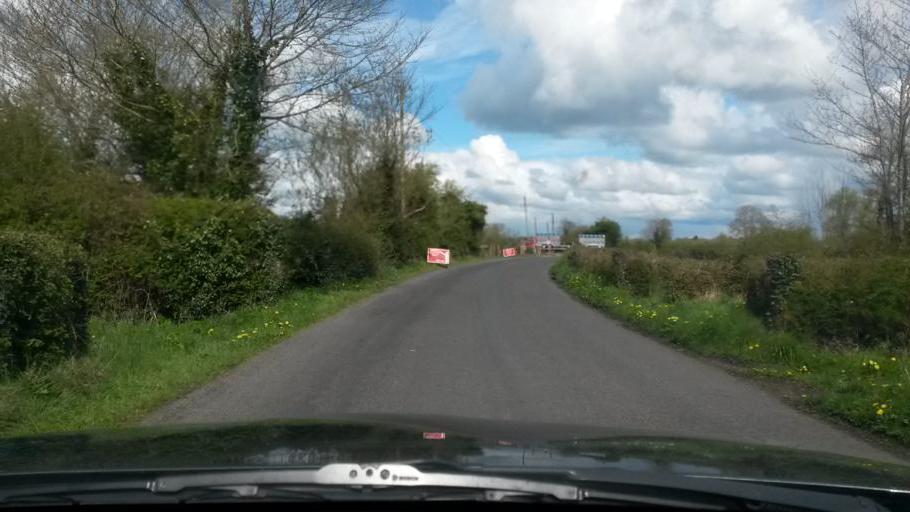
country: GB
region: Northern Ireland
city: Lisnaskea
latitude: 54.1917
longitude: -7.5139
